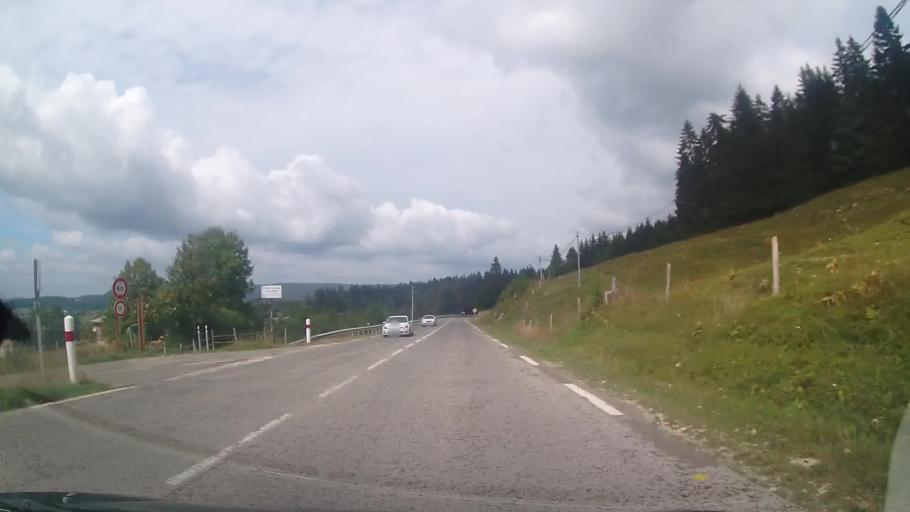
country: FR
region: Franche-Comte
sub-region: Departement du Jura
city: Les Rousses
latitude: 46.4534
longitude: 6.0710
